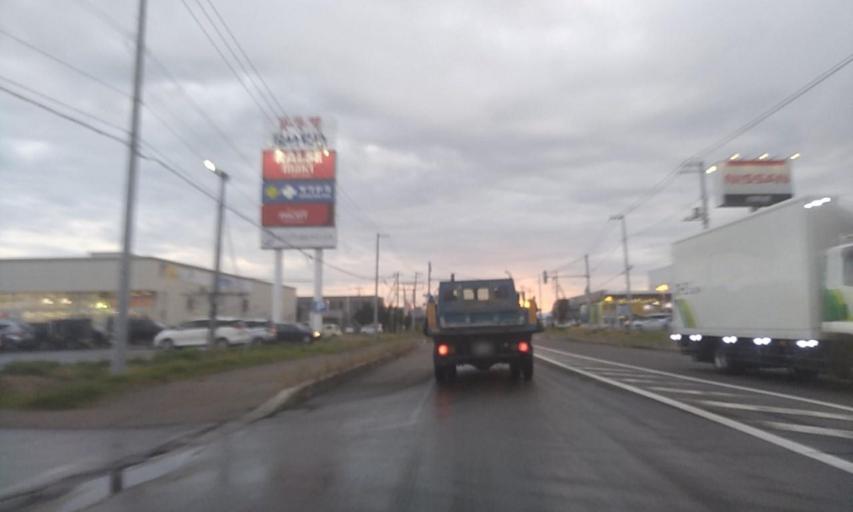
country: JP
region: Hokkaido
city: Abashiri
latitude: 43.9006
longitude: 144.6587
